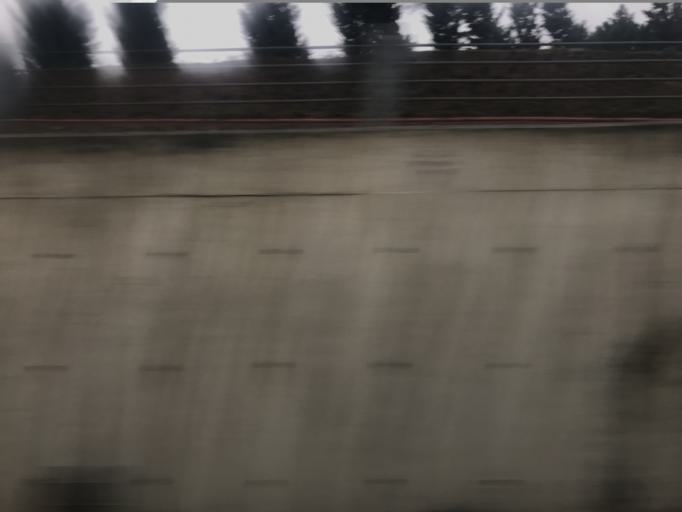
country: TR
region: Istanbul
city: UEskuedar
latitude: 41.0328
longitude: 29.0472
